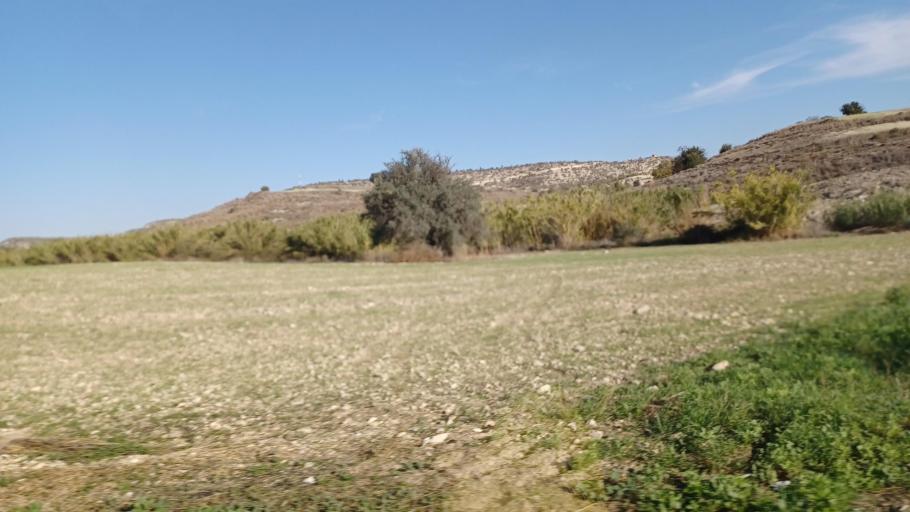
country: CY
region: Larnaka
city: Psevdas
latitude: 34.9709
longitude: 33.5213
